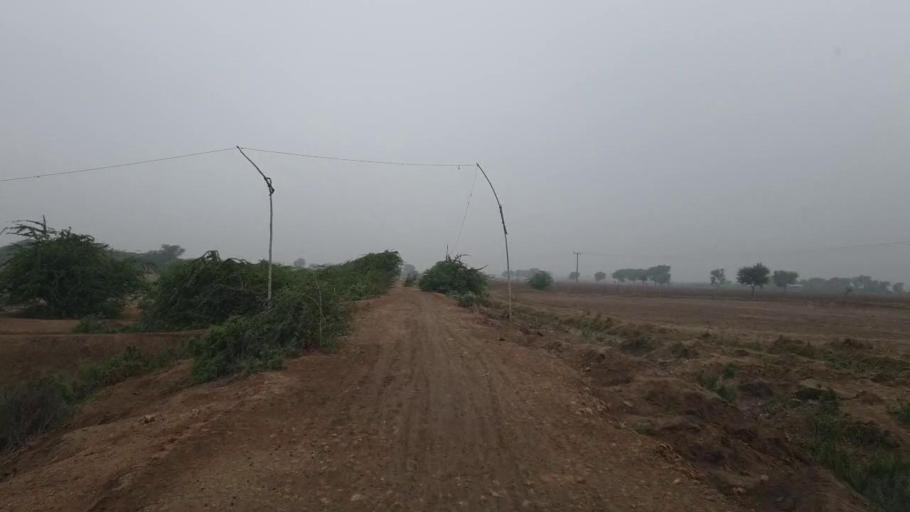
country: PK
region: Sindh
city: Badin
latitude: 24.6309
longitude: 68.6906
